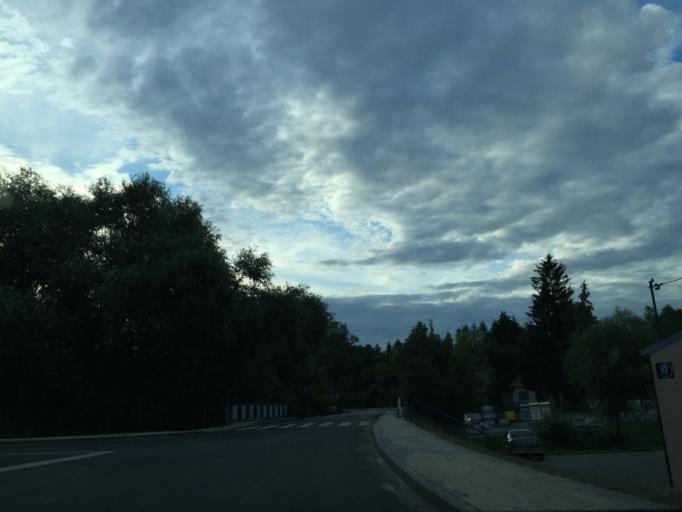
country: PL
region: Lublin Voivodeship
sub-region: Powiat lubelski
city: Lublin
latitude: 51.3128
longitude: 22.5639
